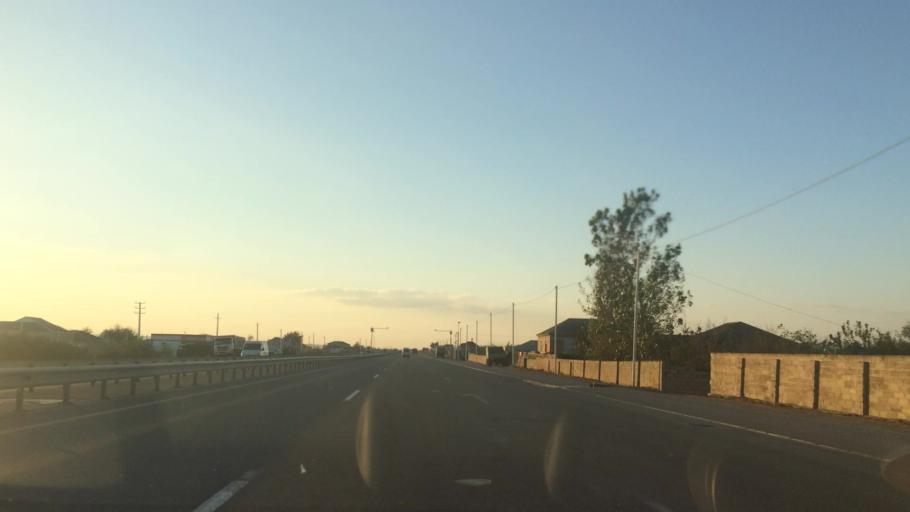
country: AZ
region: Baki
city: Qobustan
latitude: 39.9697
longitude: 49.2643
